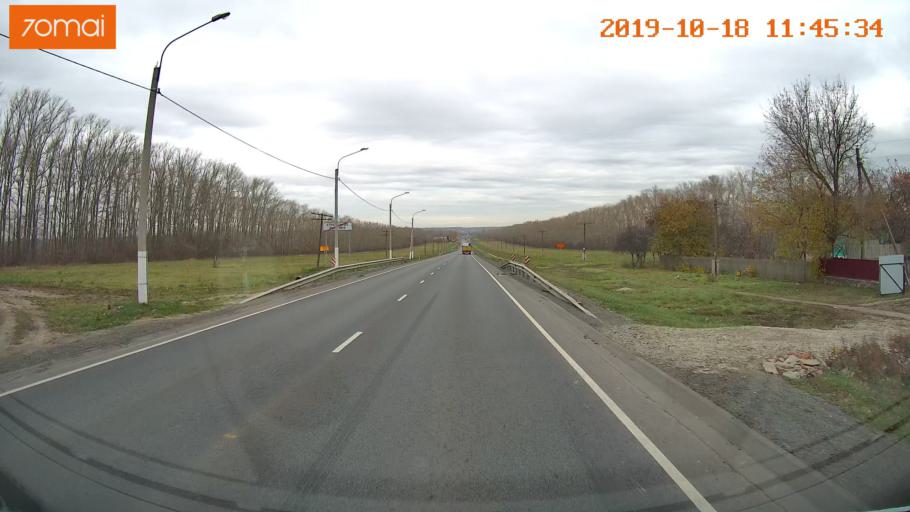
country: RU
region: Rjazan
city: Mikhaylov
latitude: 54.2115
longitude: 38.9716
